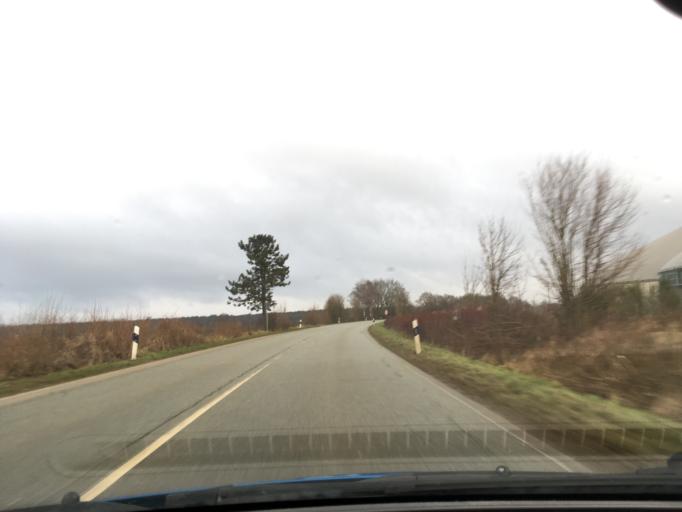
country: DE
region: Schleswig-Holstein
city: Siebeneichen
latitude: 53.5122
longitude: 10.6127
